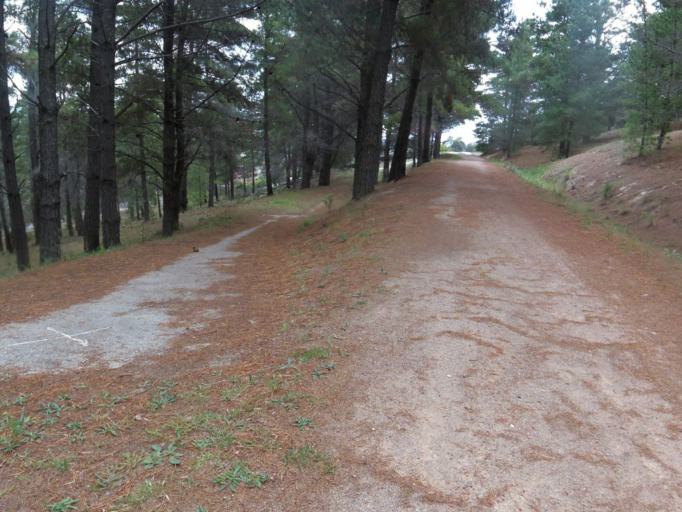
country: AU
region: Australian Capital Territory
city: Macarthur
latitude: -35.3640
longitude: 149.1135
